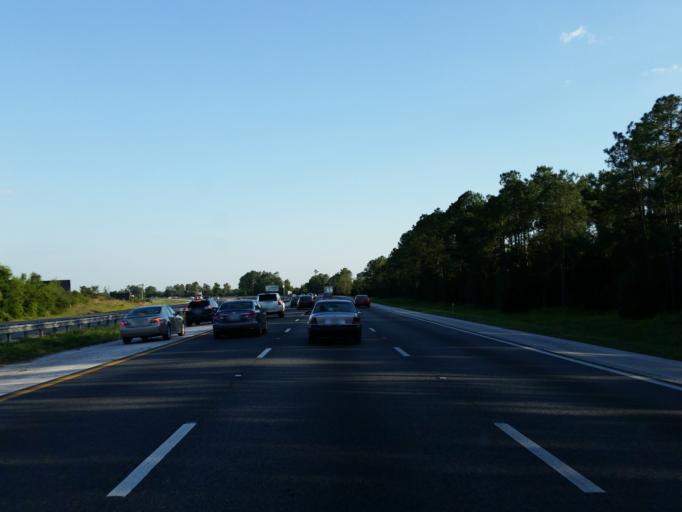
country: US
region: Florida
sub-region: Marion County
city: Ocala
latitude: 29.0824
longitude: -82.1852
